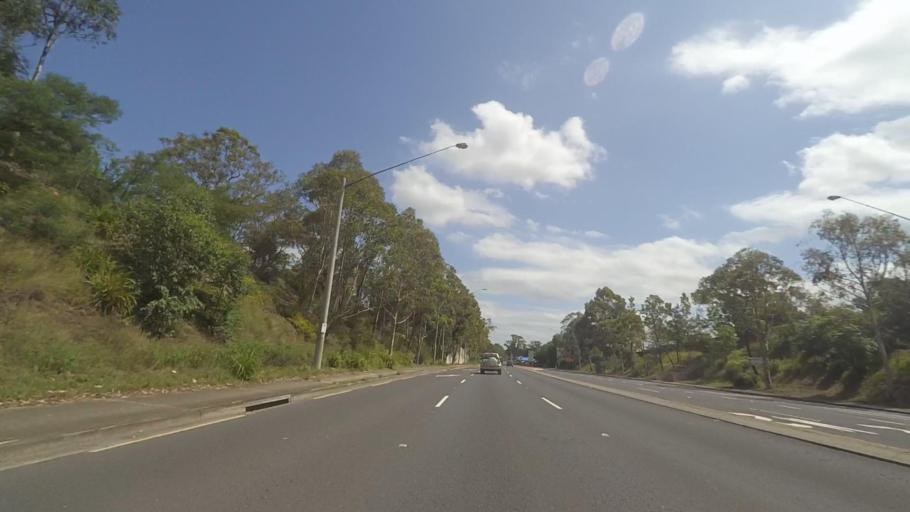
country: AU
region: New South Wales
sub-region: The Hills Shire
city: West Pennant
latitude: -33.7609
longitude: 151.0487
